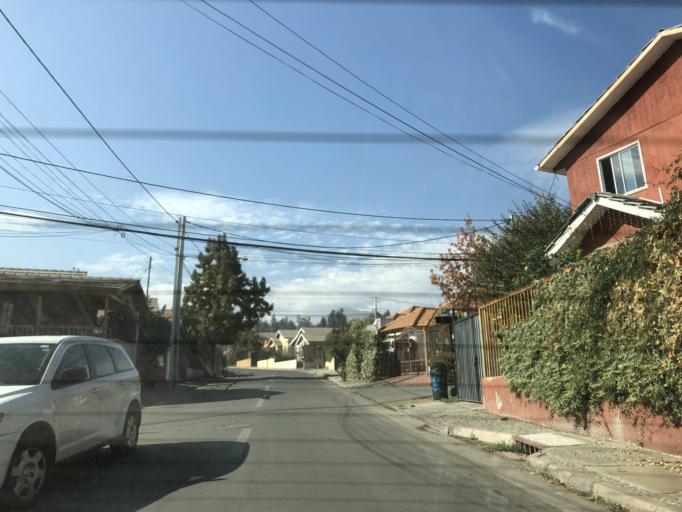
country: CL
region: Santiago Metropolitan
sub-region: Provincia de Cordillera
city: Puente Alto
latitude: -33.5716
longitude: -70.5467
